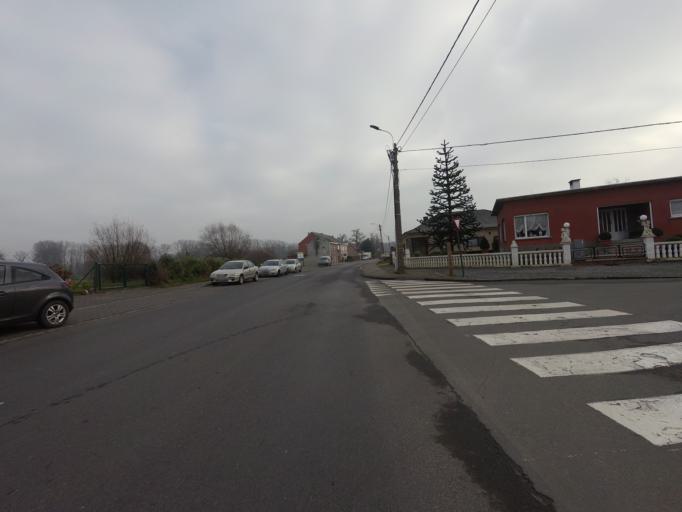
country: BE
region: Flanders
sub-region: Provincie Vlaams-Brabant
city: Galmaarden
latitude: 50.8058
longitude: 3.9603
